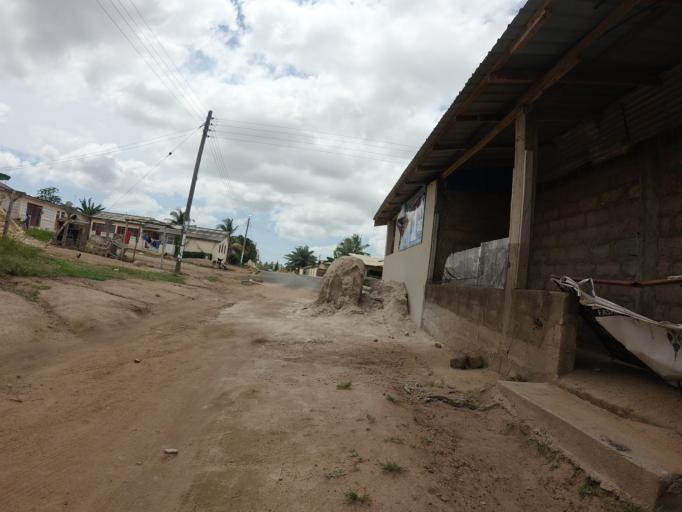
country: GH
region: Central
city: Kasoa
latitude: 5.5487
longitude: -0.3991
